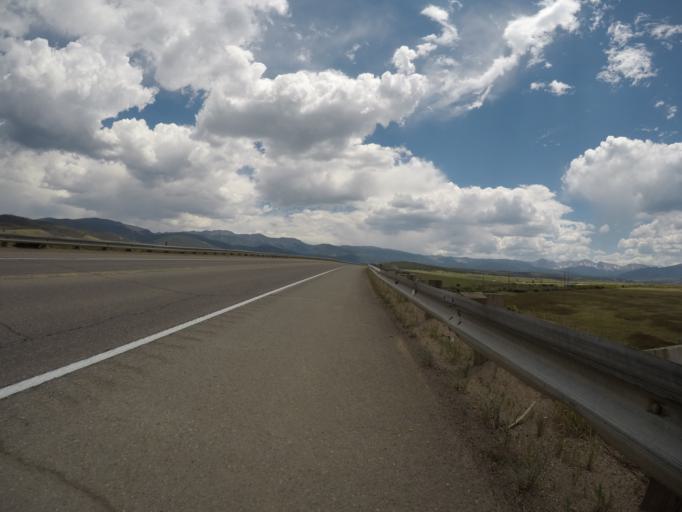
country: US
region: Colorado
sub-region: Grand County
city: Fraser
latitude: 39.9906
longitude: -105.8338
